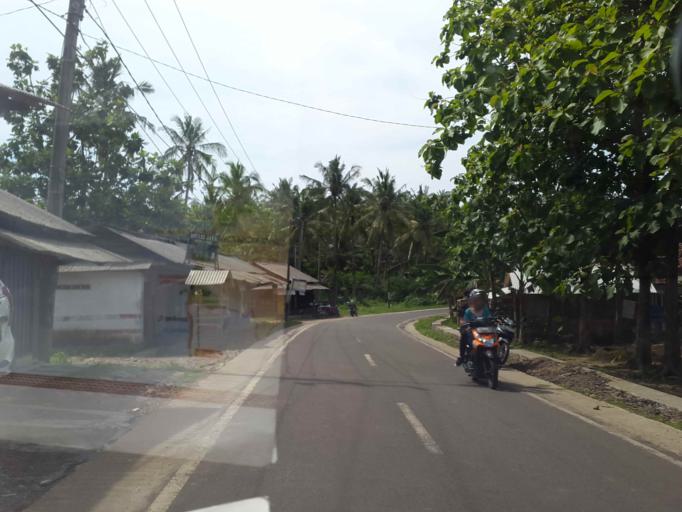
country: ID
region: Banten
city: Citeureup
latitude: -6.5313
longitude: 105.7088
